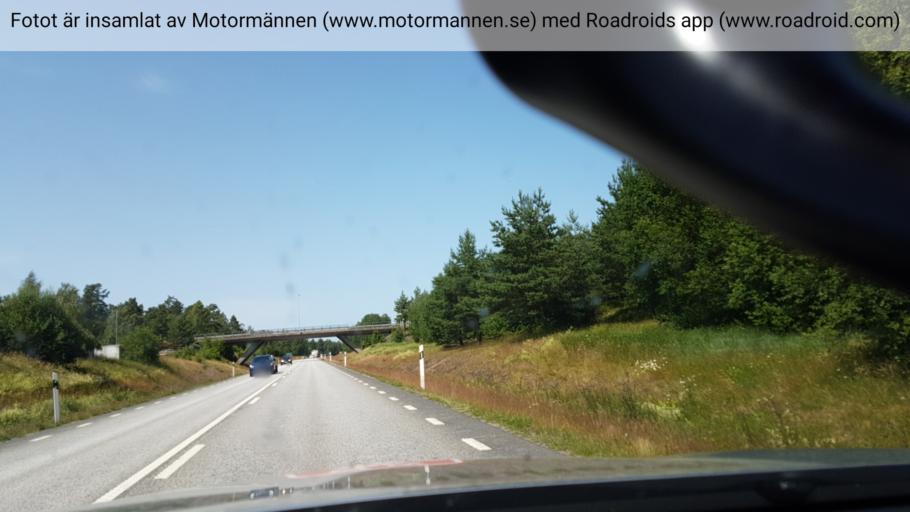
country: SE
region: Joenkoeping
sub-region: Eksjo Kommun
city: Eksjoe
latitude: 57.6627
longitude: 14.9561
